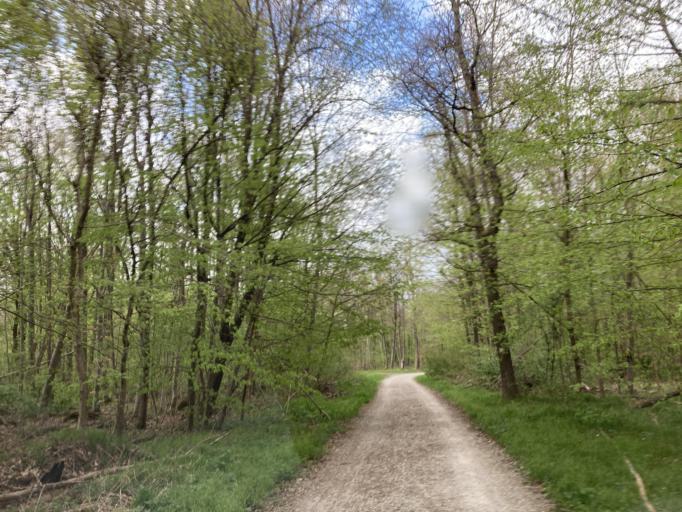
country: DE
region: Baden-Wuerttemberg
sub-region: Tuebingen Region
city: Wannweil
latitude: 48.5120
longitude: 9.1374
